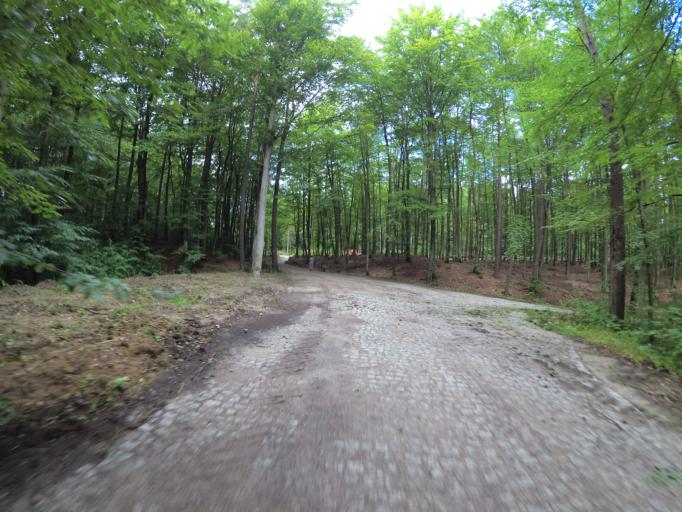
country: PL
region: Pomeranian Voivodeship
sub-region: Powiat wejherowski
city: Bojano
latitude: 54.5070
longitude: 18.4184
